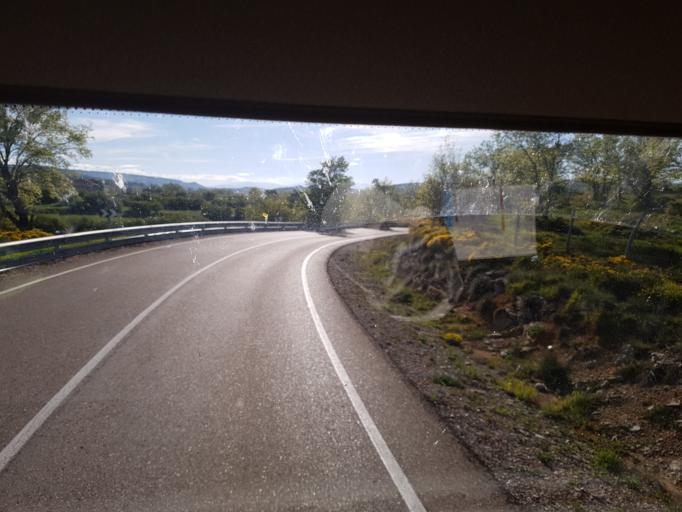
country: ES
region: Cantabria
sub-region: Provincia de Cantabria
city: San Pedro del Romeral
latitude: 42.9728
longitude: -3.7827
